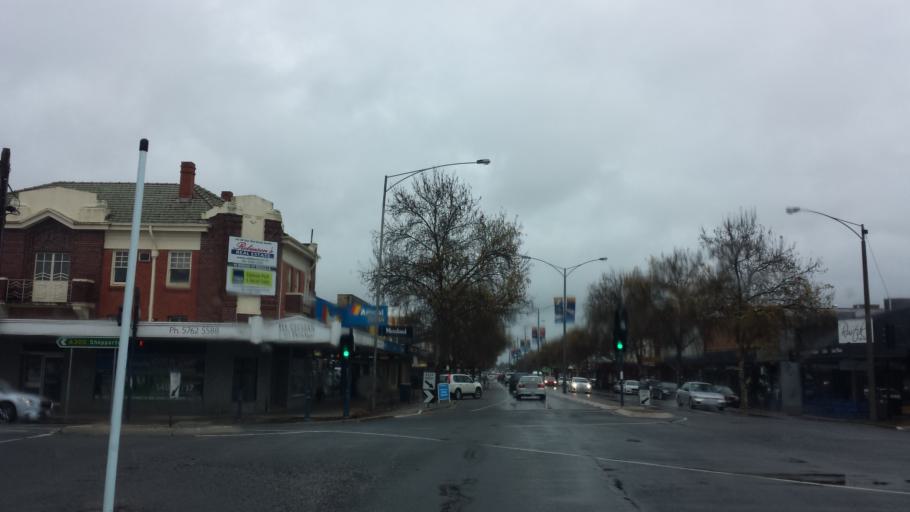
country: AU
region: Victoria
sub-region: Benalla
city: Benalla
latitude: -36.5518
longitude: 145.9830
